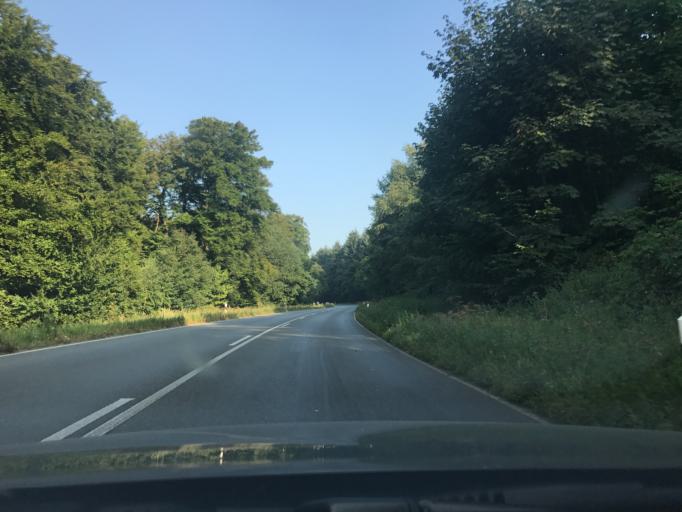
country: DE
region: North Rhine-Westphalia
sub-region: Regierungsbezirk Dusseldorf
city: Kleve
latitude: 51.7713
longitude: 6.1559
